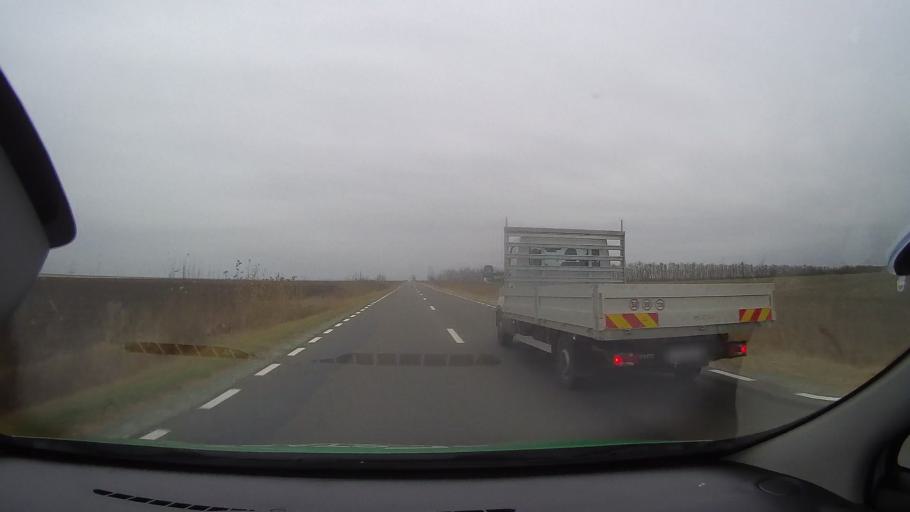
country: RO
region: Ialomita
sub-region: Comuna Gheorghe Lazar
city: Gheorghe Lazar
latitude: 44.6688
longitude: 27.4170
